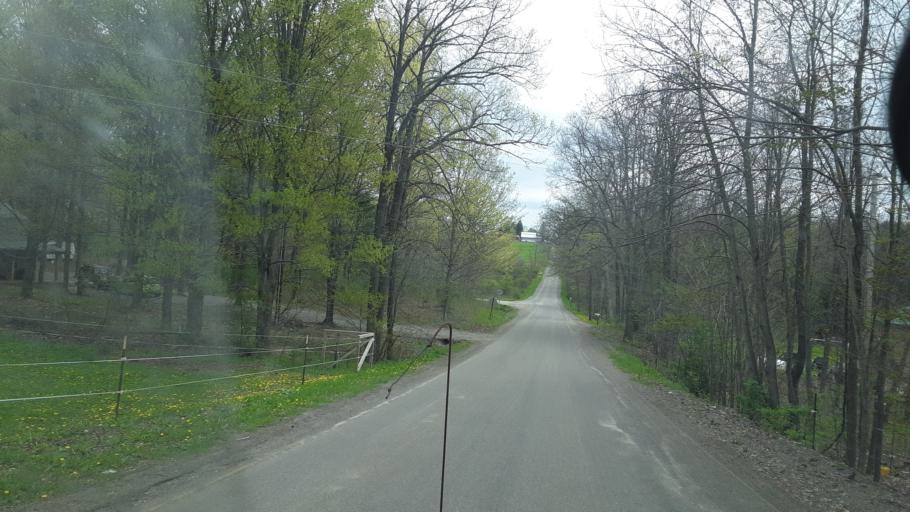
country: US
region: New York
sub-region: Steuben County
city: Addison
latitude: 42.0928
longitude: -77.2996
